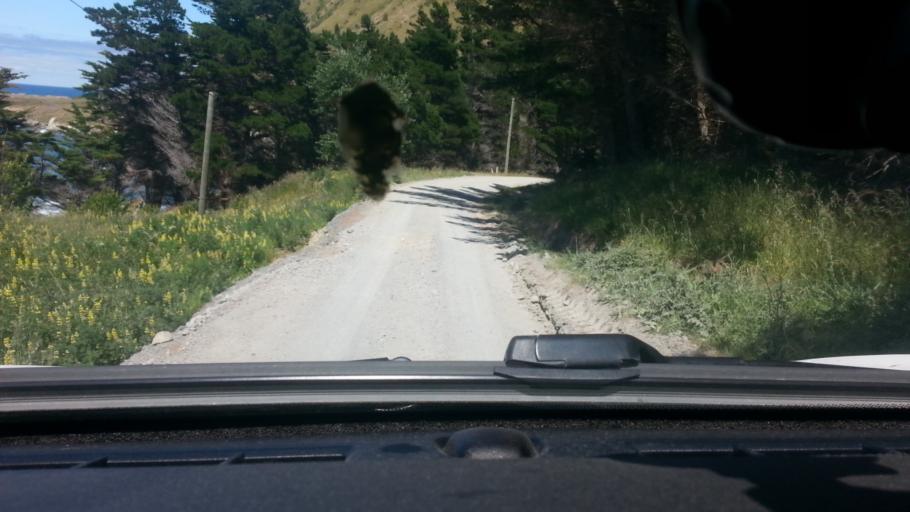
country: NZ
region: Wellington
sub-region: South Wairarapa District
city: Waipawa
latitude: -41.4947
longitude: 175.5346
